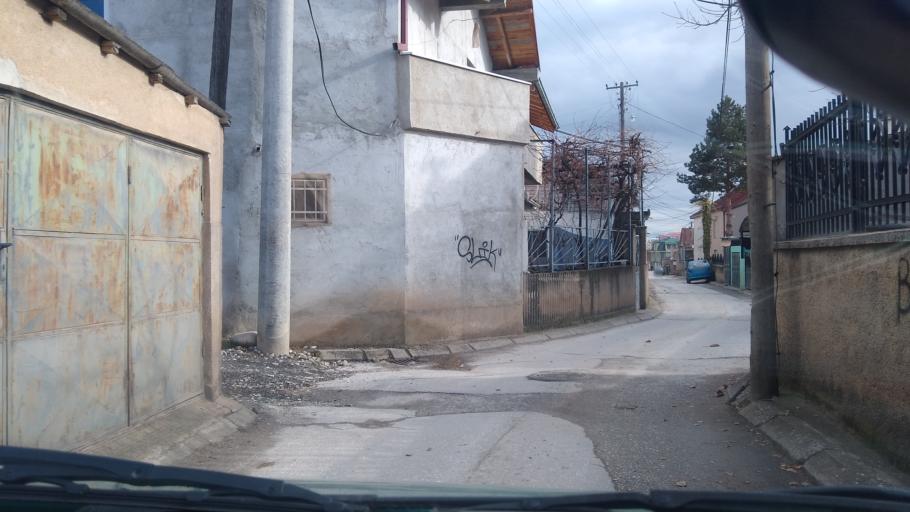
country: MK
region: Bitola
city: Bitola
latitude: 41.0283
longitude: 21.3185
